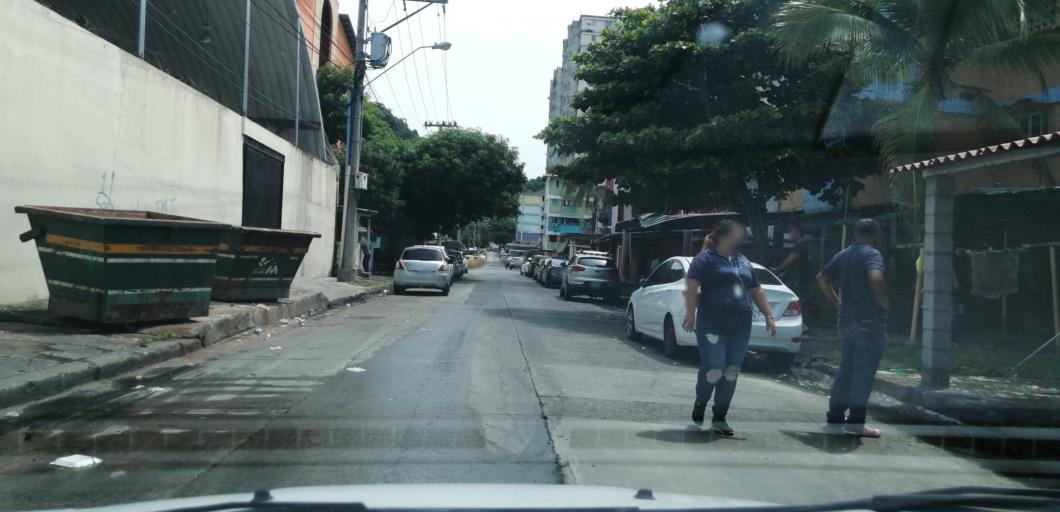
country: PA
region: Panama
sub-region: Distrito de Panama
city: Ancon
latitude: 8.9486
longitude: -79.5480
